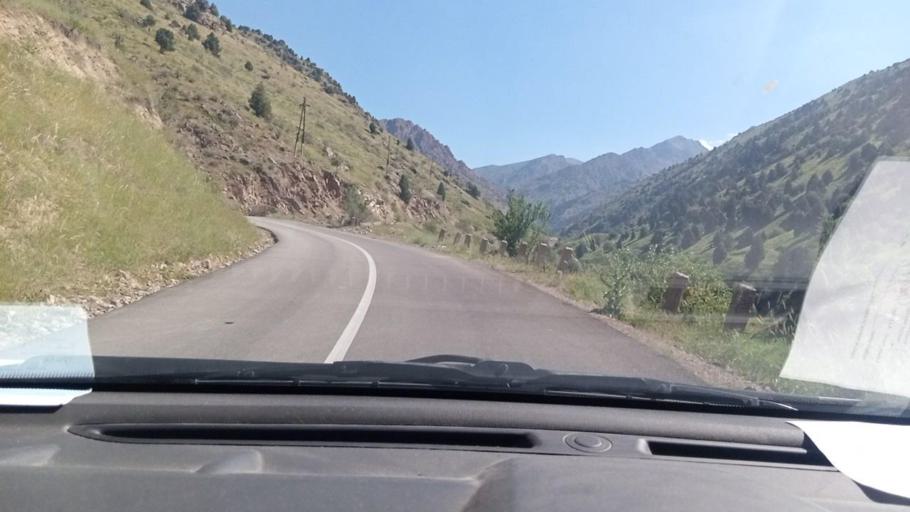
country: UZ
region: Toshkent
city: Yangiobod
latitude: 41.1288
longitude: 70.1107
